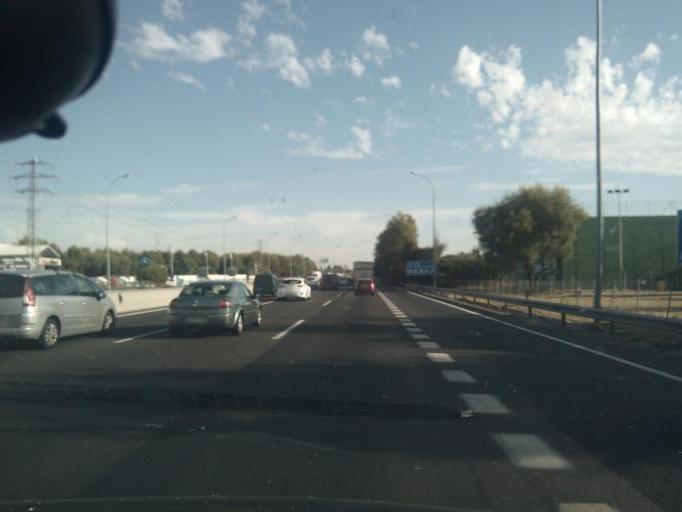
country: ES
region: Madrid
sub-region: Provincia de Madrid
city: Pinto
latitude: 40.2556
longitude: -3.6903
